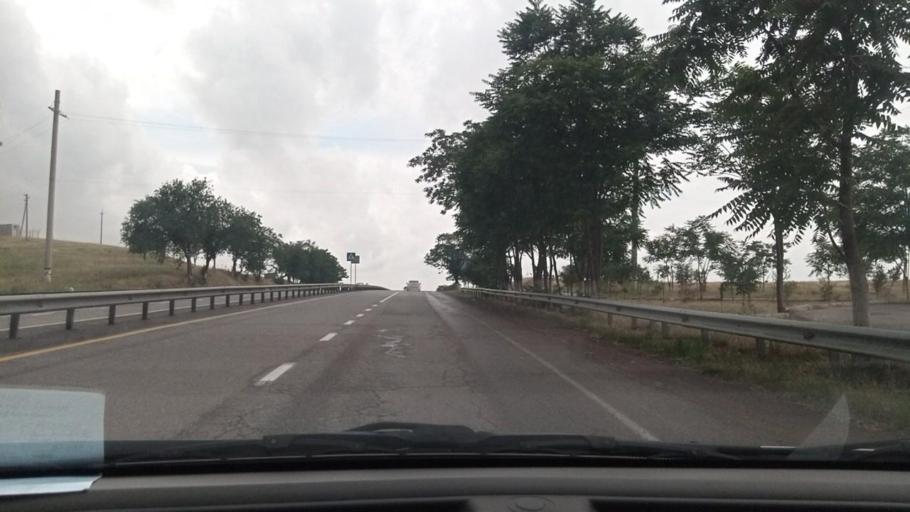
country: UZ
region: Toshkent
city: Ohangaron
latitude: 40.9606
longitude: 69.5587
